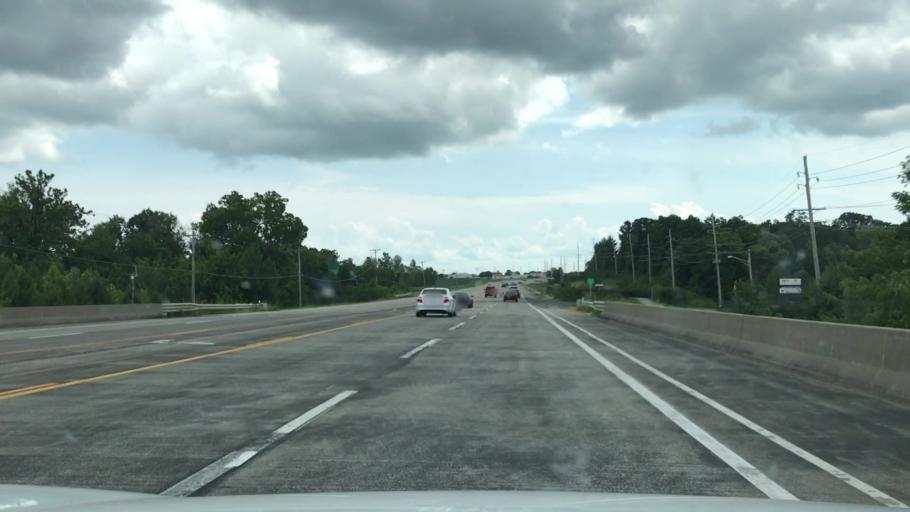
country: US
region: Missouri
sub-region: Saint Charles County
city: Weldon Spring
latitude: 38.7406
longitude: -90.6952
